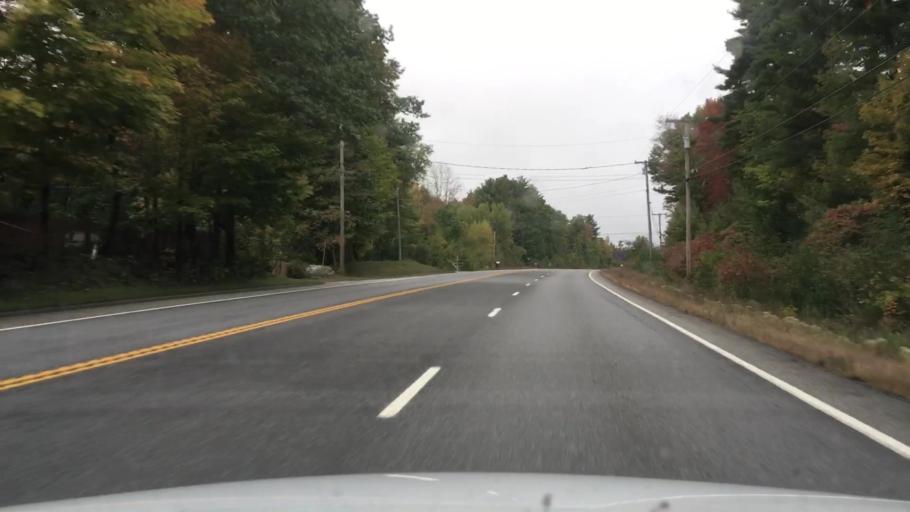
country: US
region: Maine
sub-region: Cumberland County
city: New Gloucester
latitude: 43.9740
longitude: -70.3651
